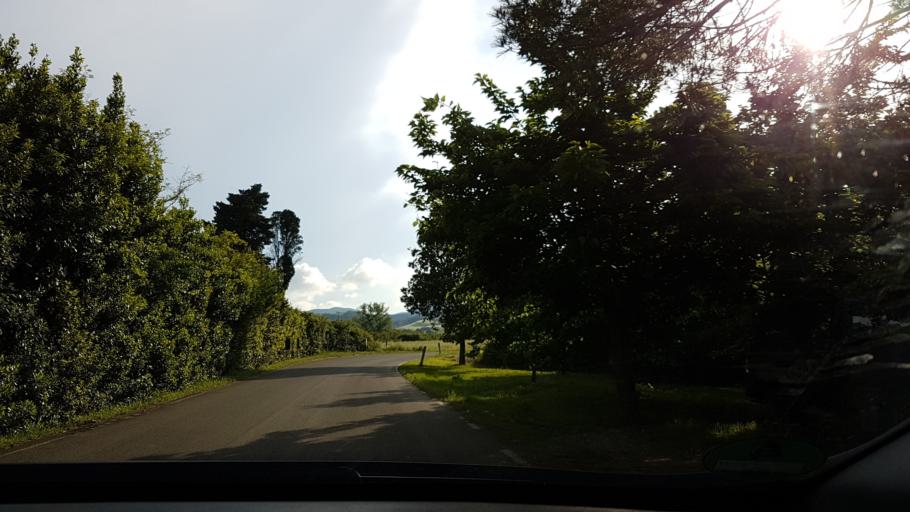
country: IT
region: Tuscany
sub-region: Province of Pisa
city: Chianni
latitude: 43.4814
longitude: 10.6839
